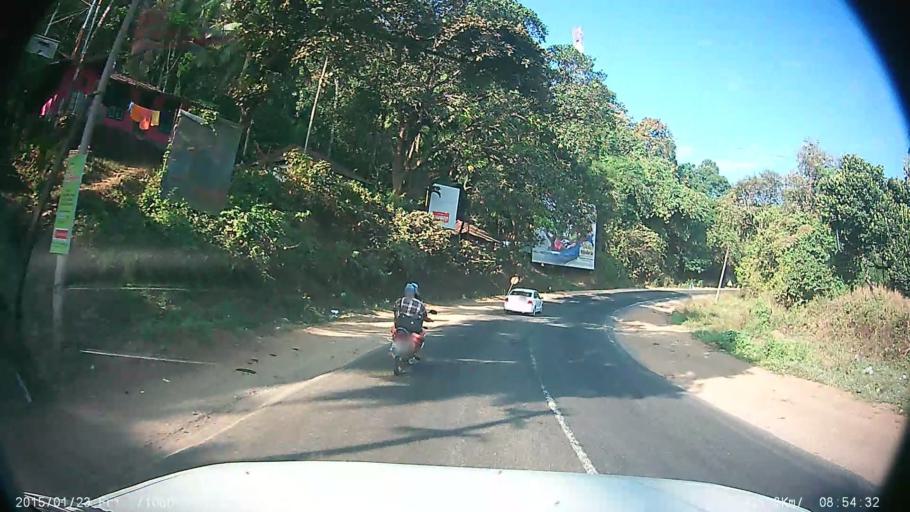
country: IN
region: Kerala
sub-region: Thrissur District
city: Chelakara
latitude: 10.5732
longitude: 76.3865
